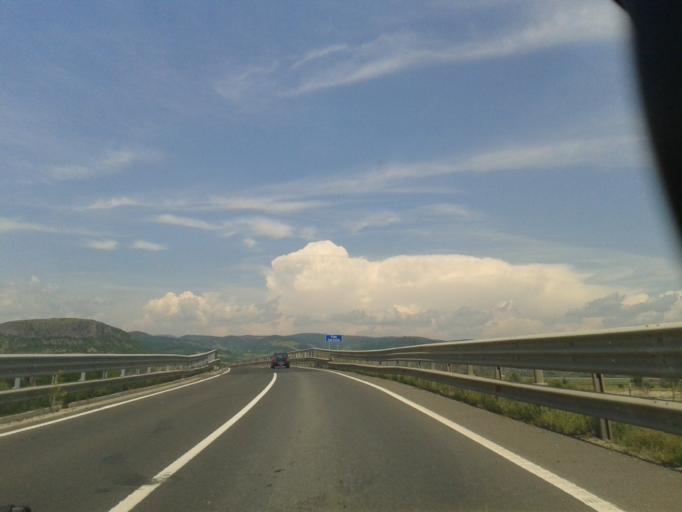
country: RO
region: Hunedoara
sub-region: Oras Simeria
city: Simeria
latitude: 45.8375
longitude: 23.0442
